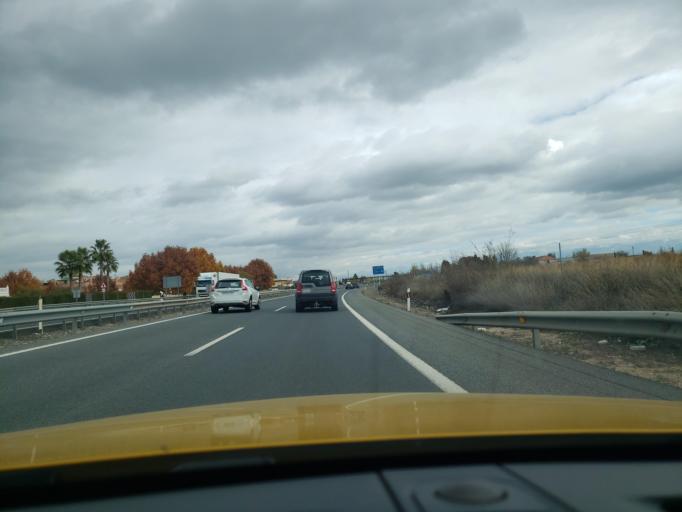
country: ES
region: Andalusia
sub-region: Provincia de Granada
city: Cijuela
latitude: 37.1951
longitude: -3.8157
